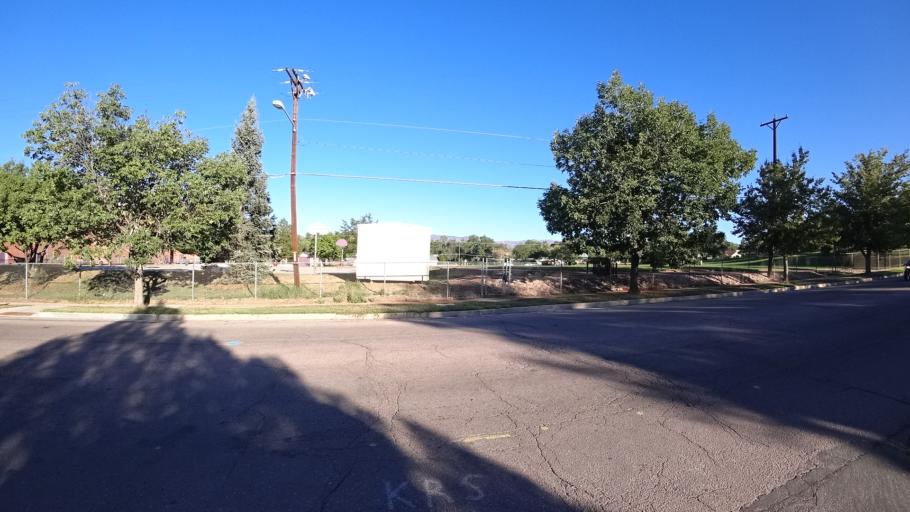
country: US
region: Colorado
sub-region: El Paso County
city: Colorado Springs
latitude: 38.8436
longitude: -104.8522
